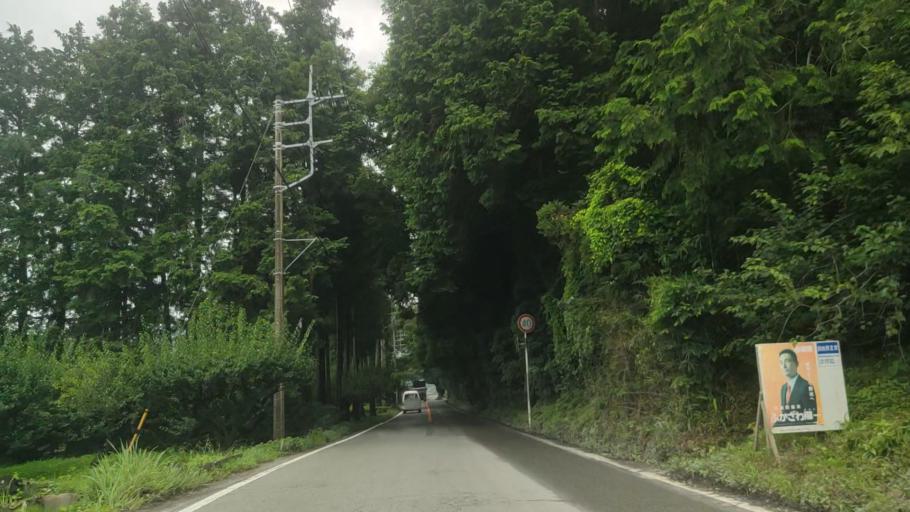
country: JP
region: Shizuoka
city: Fujinomiya
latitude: 35.2188
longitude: 138.5426
